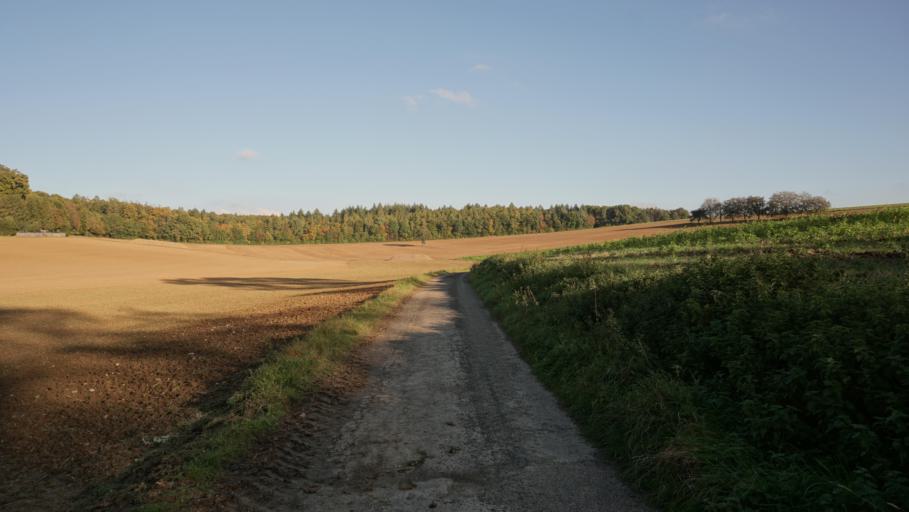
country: DE
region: Baden-Wuerttemberg
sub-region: Karlsruhe Region
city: Billigheim
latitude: 49.3616
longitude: 9.2314
